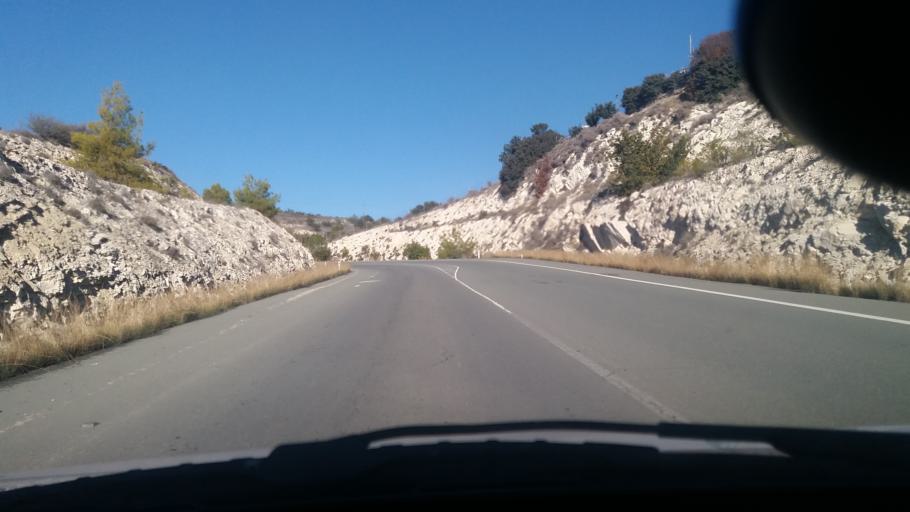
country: CY
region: Larnaka
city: Kofinou
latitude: 34.8538
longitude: 33.4486
